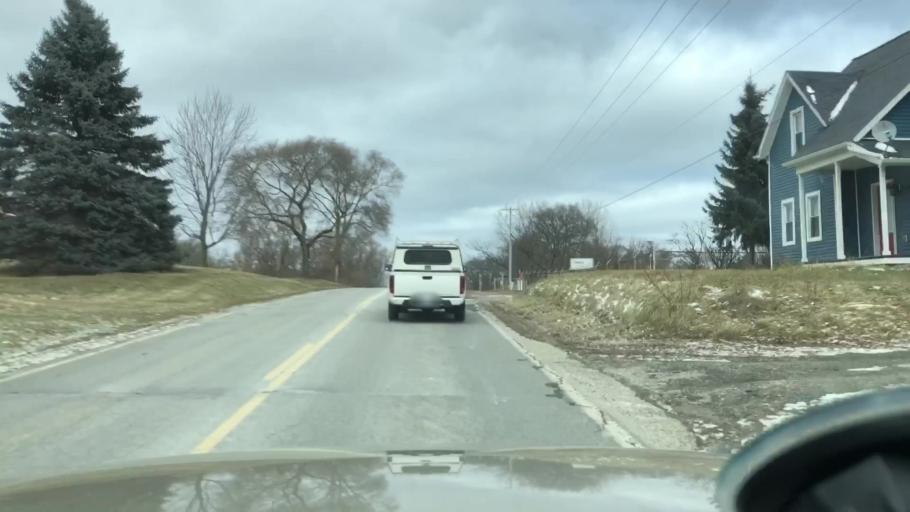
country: US
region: Michigan
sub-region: Jackson County
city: Jackson
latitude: 42.2729
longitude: -84.3649
